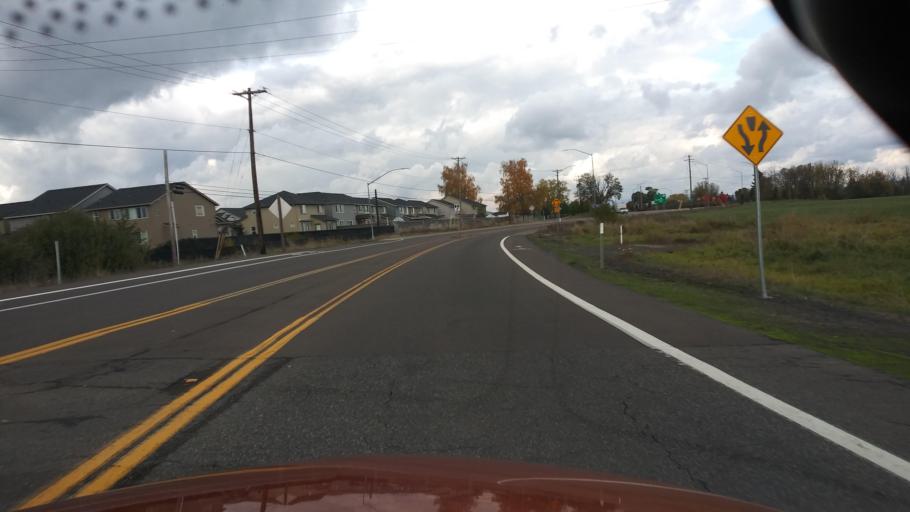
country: US
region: Oregon
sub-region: Washington County
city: Forest Grove
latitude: 45.5369
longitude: -123.1072
